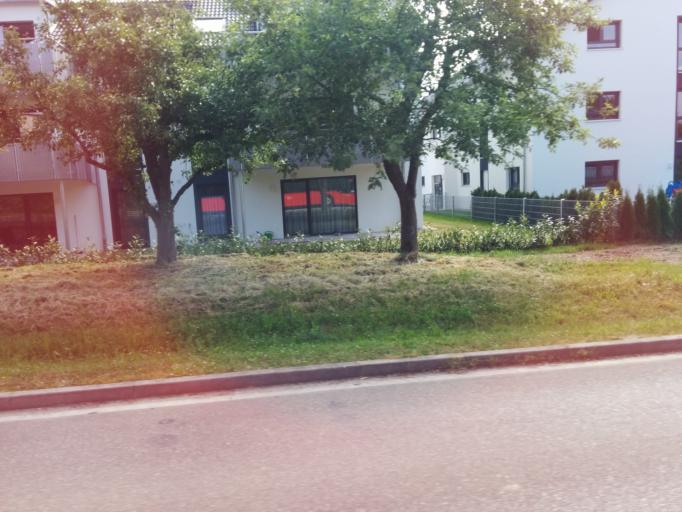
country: DE
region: Baden-Wuerttemberg
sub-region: Regierungsbezirk Stuttgart
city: Untergruppenbach
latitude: 49.0969
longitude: 9.2734
